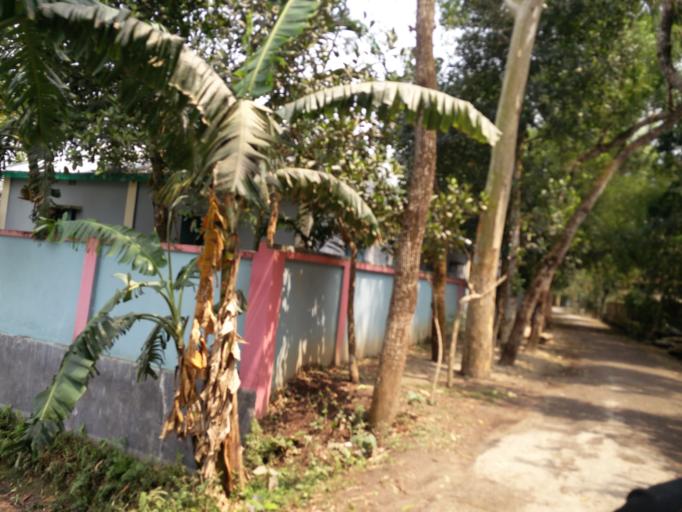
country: BD
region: Dhaka
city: Sherpur
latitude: 24.9337
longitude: 90.1648
